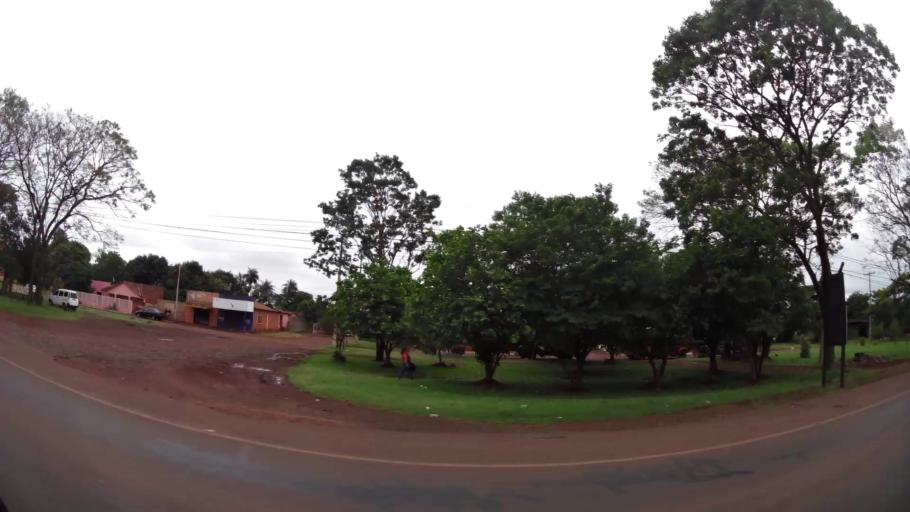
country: PY
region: Alto Parana
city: Los Cedrales
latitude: -25.4889
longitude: -54.8067
